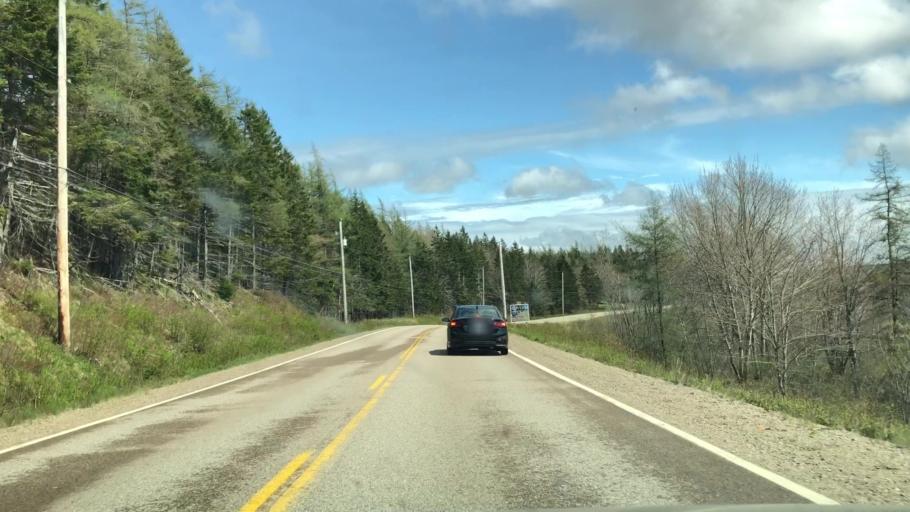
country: CA
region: Nova Scotia
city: Antigonish
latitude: 45.1914
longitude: -61.9915
